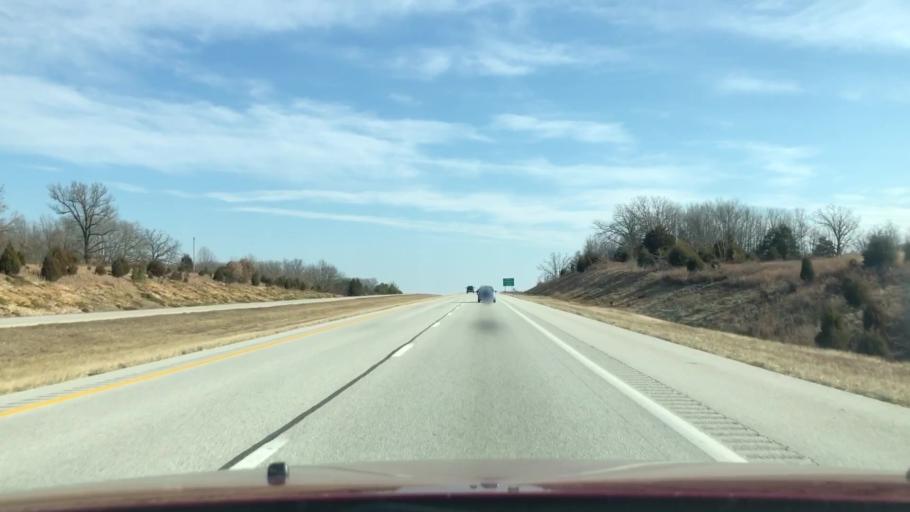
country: US
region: Missouri
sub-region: Webster County
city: Seymour
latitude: 37.1620
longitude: -92.8892
